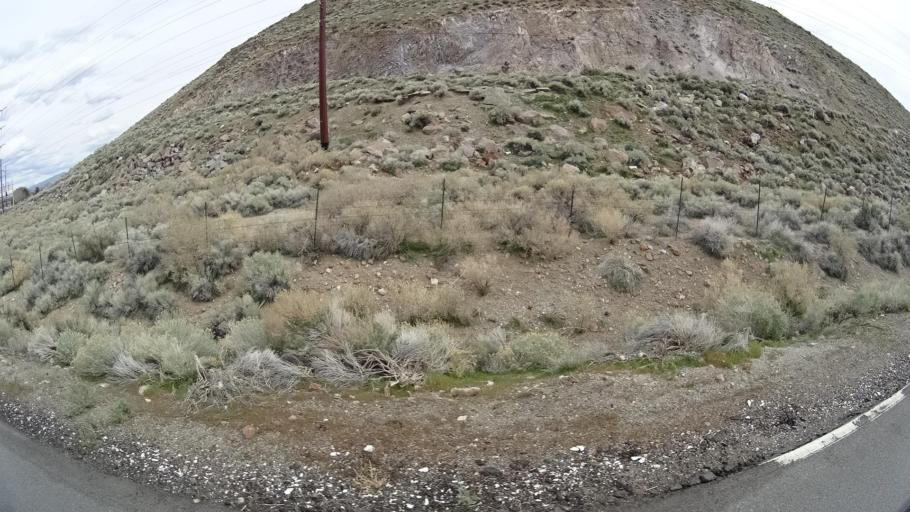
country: US
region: Nevada
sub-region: Washoe County
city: Sparks
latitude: 39.4746
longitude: -119.7632
